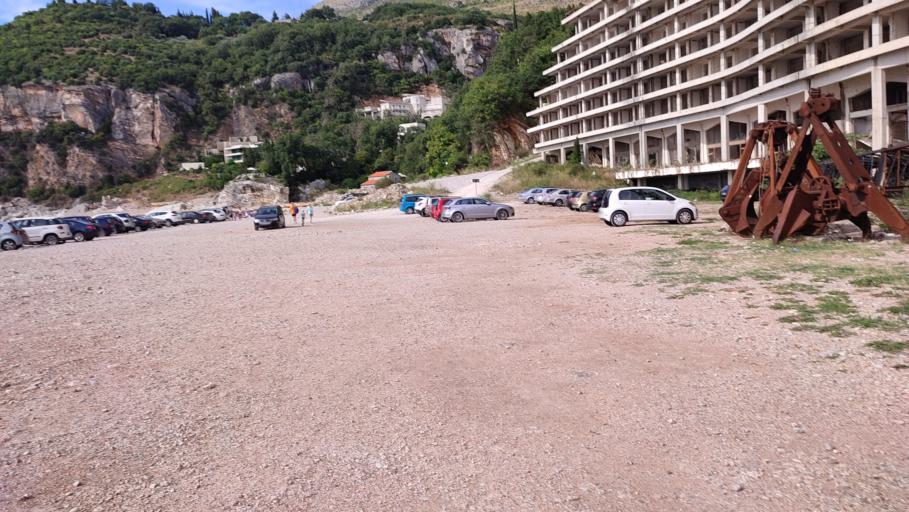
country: ME
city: Petrovac na Moru
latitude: 42.2101
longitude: 18.9260
